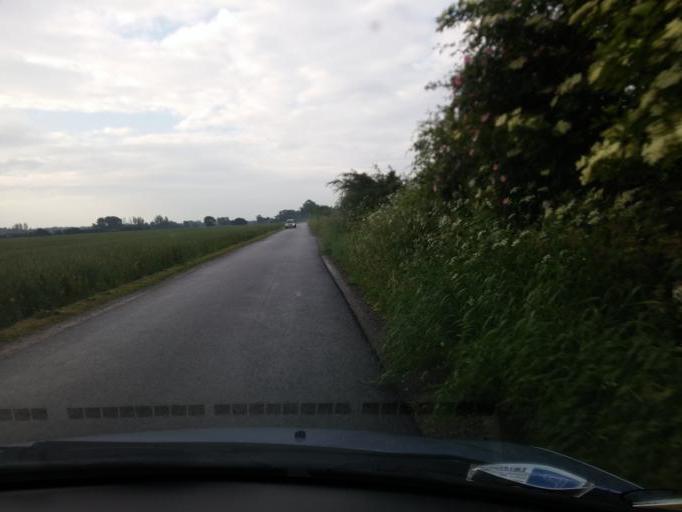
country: DK
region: South Denmark
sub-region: Kerteminde Kommune
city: Munkebo
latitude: 55.4124
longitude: 10.5599
